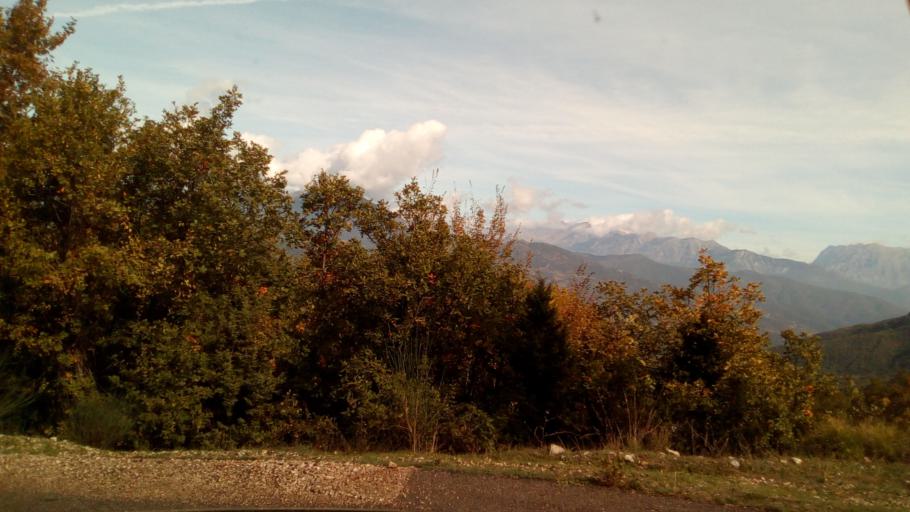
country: GR
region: West Greece
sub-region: Nomos Achaias
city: Kamarai
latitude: 38.4778
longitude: 22.0252
